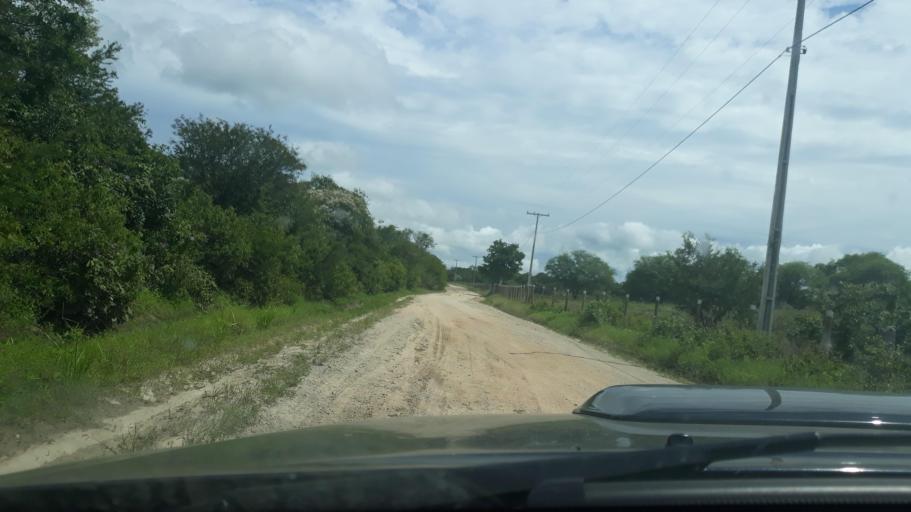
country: BR
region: Bahia
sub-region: Riacho De Santana
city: Riacho de Santana
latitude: -13.8810
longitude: -43.0211
